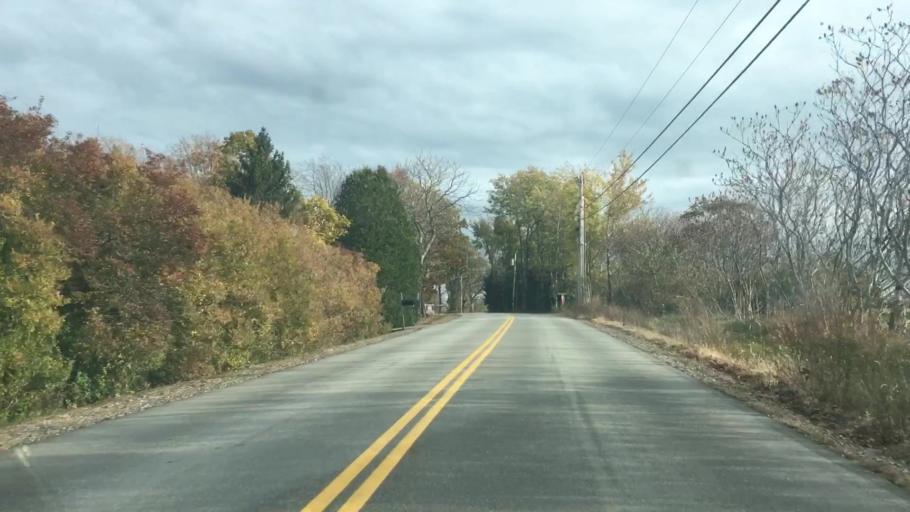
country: US
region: Maine
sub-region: York County
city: Springvale
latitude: 43.4600
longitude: -70.8223
